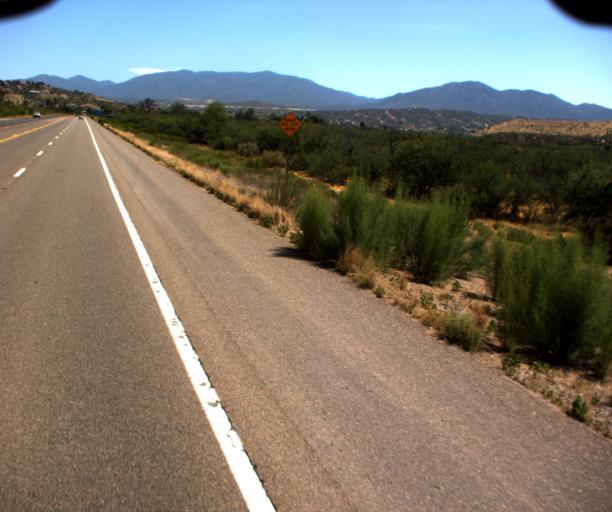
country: US
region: Arizona
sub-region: Gila County
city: Claypool
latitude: 33.4322
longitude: -110.8280
